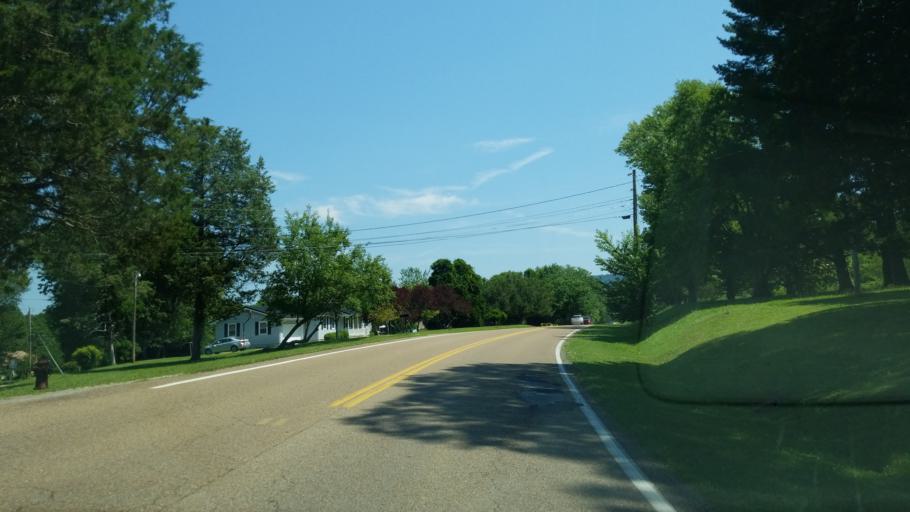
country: US
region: Tennessee
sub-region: Hamilton County
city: Collegedale
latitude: 35.1118
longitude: -85.0466
